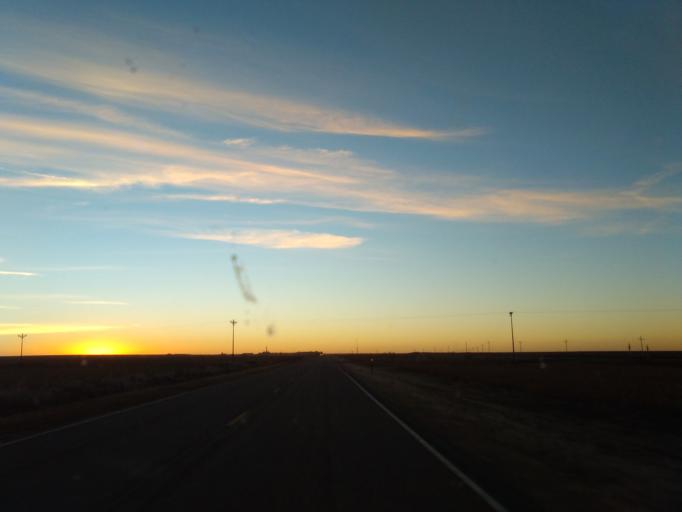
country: US
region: Kansas
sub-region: Wallace County
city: Sharon Springs
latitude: 38.8567
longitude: -102.0510
